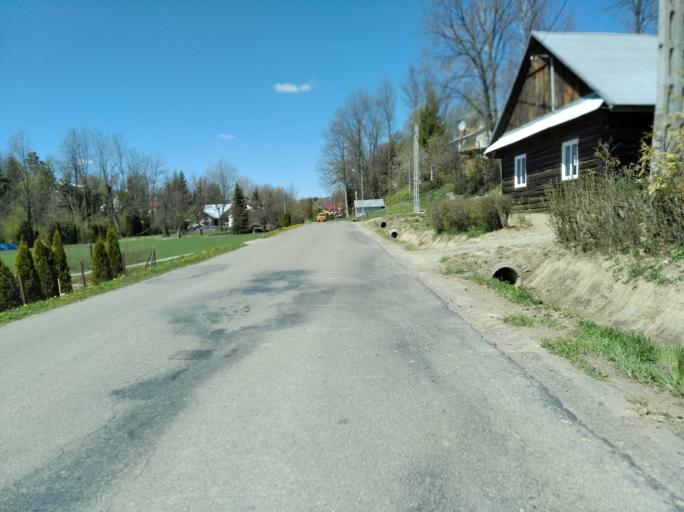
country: PL
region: Subcarpathian Voivodeship
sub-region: Powiat brzozowski
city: Jablonka
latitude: 49.7094
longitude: 22.1431
